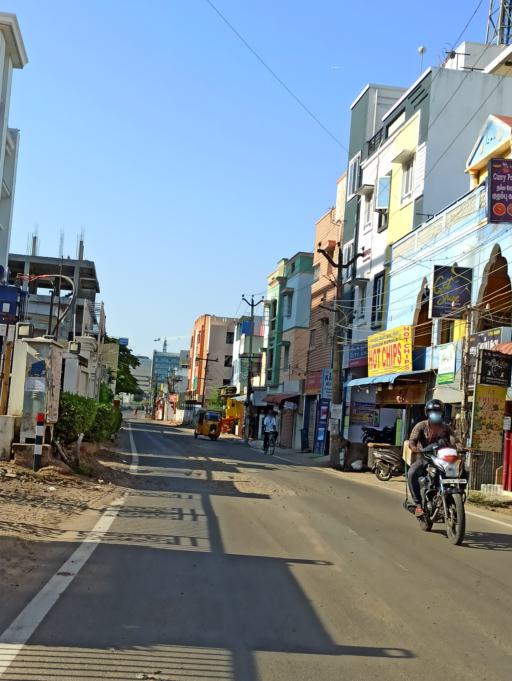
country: IN
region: Tamil Nadu
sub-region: Kancheepuram
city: Manappakkam
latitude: 13.0246
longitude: 80.1678
